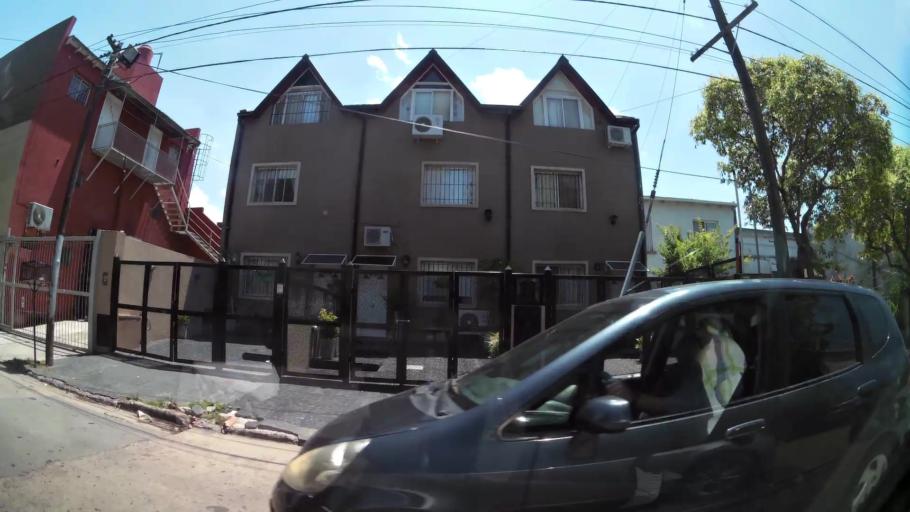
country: AR
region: Buenos Aires
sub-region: Partido de Tigre
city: Tigre
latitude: -34.4223
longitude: -58.5912
